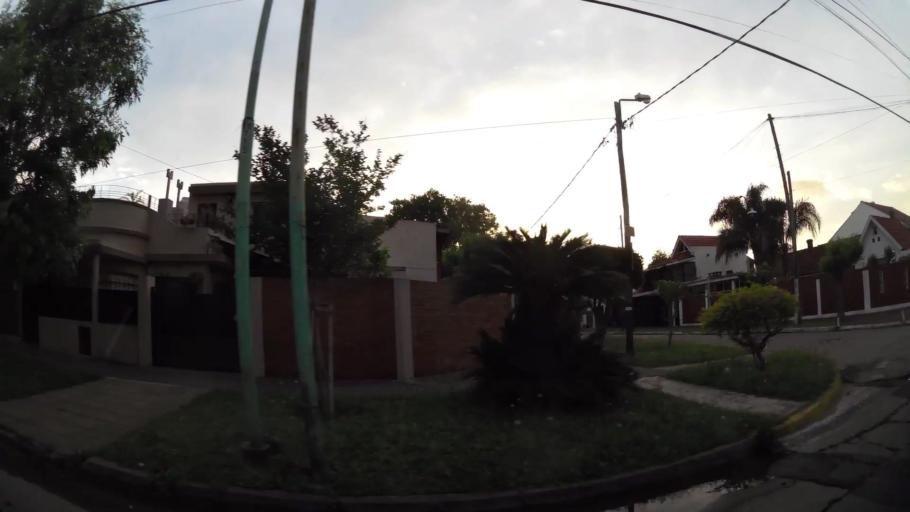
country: AR
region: Buenos Aires
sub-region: Partido de Lomas de Zamora
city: Lomas de Zamora
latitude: -34.7666
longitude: -58.3874
